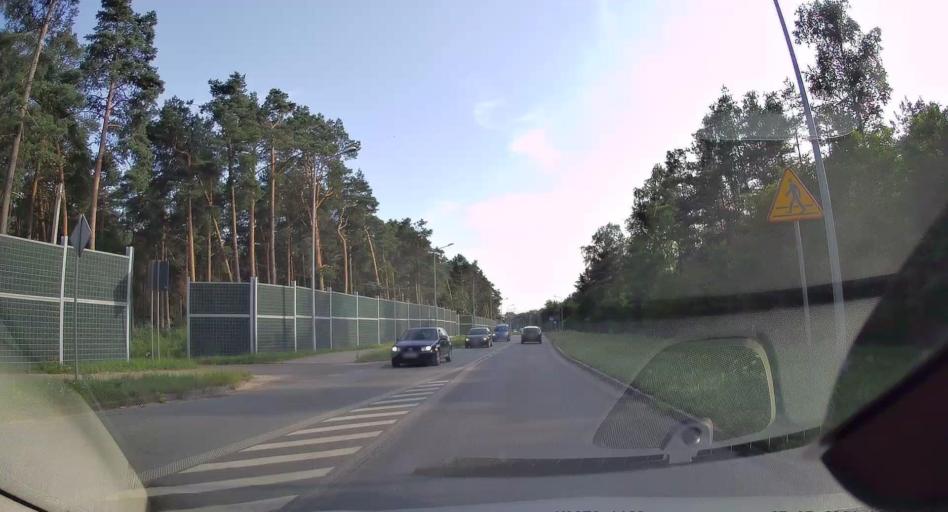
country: PL
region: Swietokrzyskie
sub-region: Powiat konecki
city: Konskie
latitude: 51.1219
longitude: 20.3546
